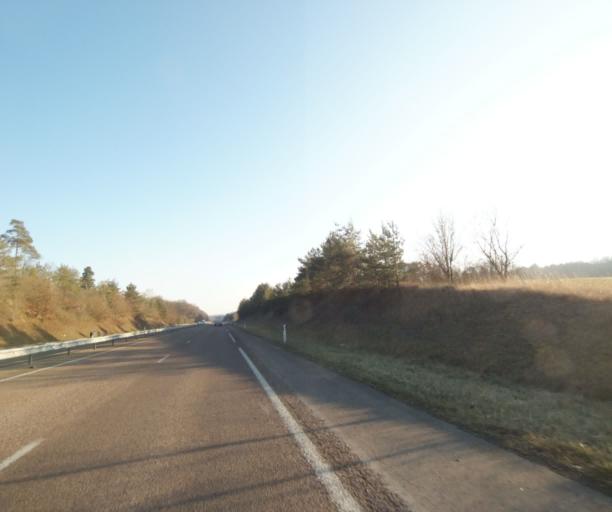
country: FR
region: Champagne-Ardenne
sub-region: Departement de la Haute-Marne
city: Chevillon
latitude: 48.5075
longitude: 5.0980
